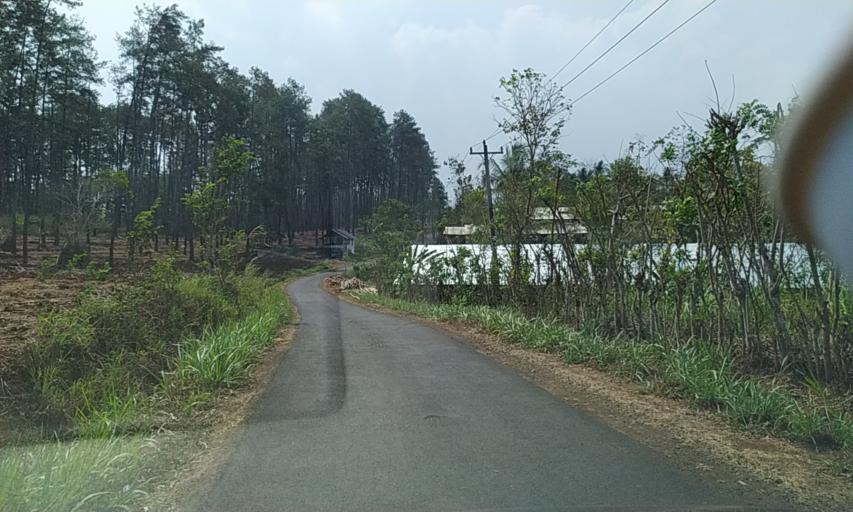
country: ID
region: Central Java
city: Rungkang
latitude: -7.4453
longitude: 108.8549
